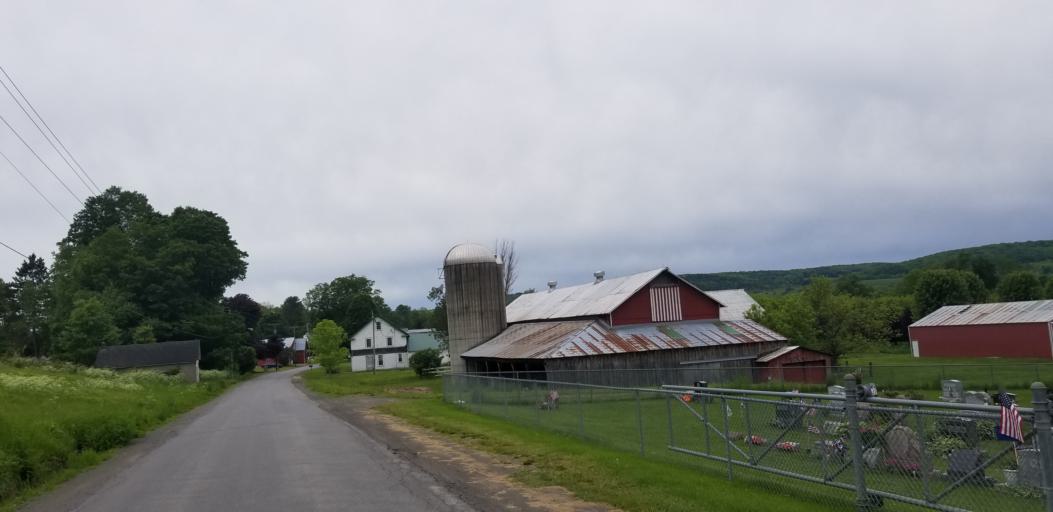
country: US
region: New York
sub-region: Oneida County
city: Waterville
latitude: 42.8469
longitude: -75.2329
